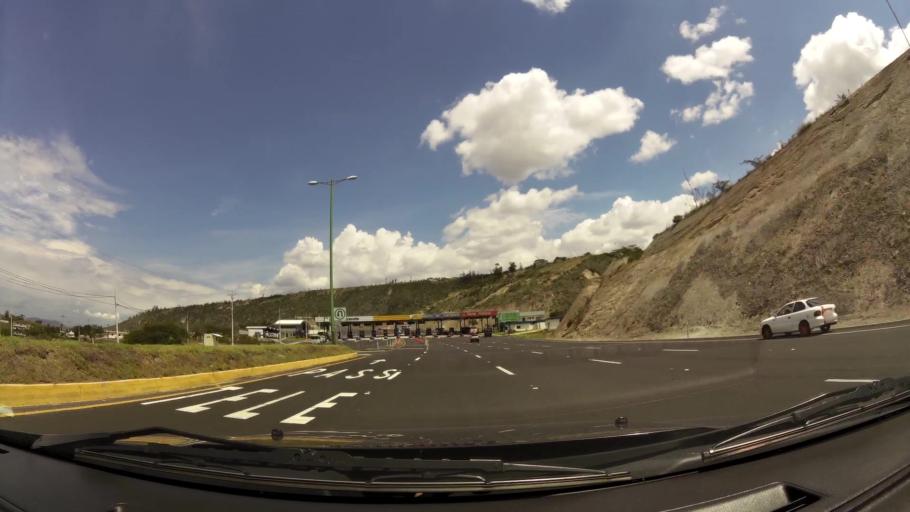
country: EC
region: Pichincha
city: Quito
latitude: -0.0981
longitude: -78.4059
